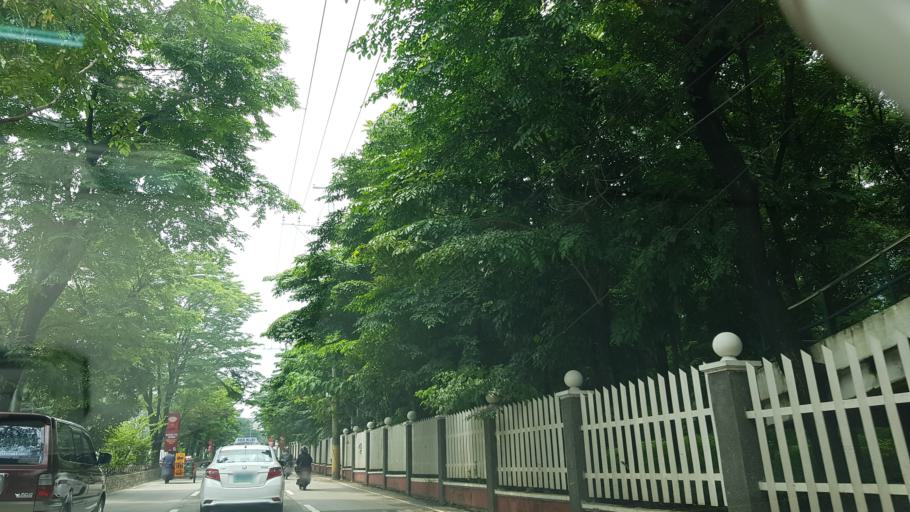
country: PH
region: Metro Manila
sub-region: Makati City
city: Makati City
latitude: 14.5328
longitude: 121.0410
